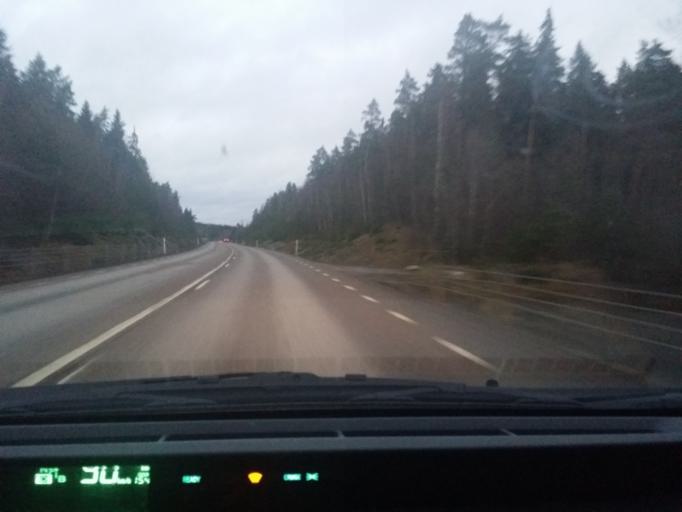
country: SE
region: Soedermanland
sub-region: Eskilstuna Kommun
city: Kvicksund
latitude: 59.5180
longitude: 16.3220
